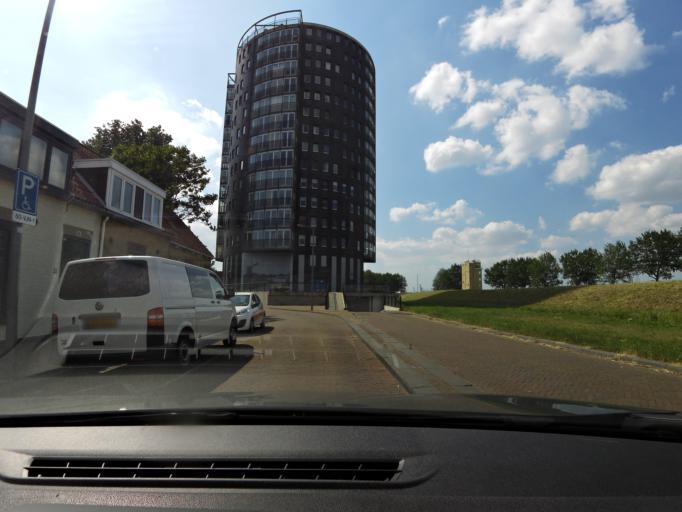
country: NL
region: South Holland
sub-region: Gemeente Schiedam
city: Schiedam
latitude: 51.8933
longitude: 4.3910
